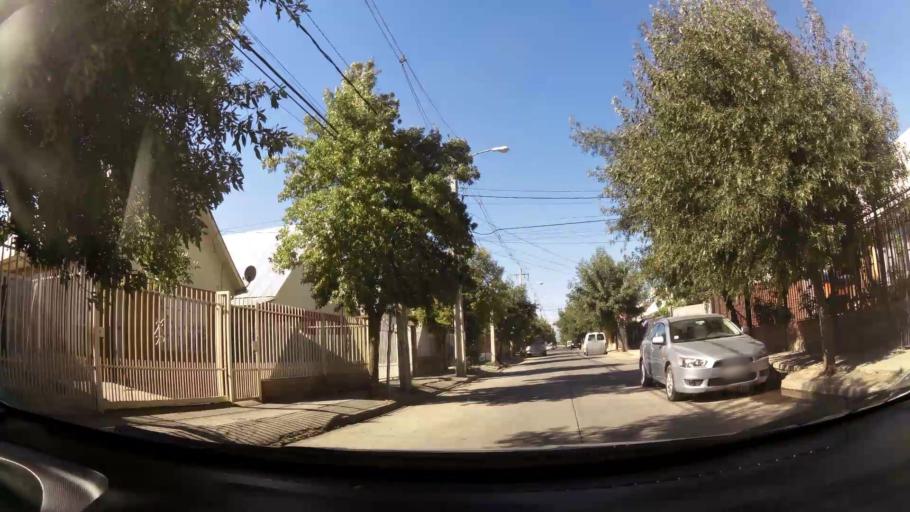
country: CL
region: O'Higgins
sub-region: Provincia de Cachapoal
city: Rancagua
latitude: -34.1840
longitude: -70.7727
